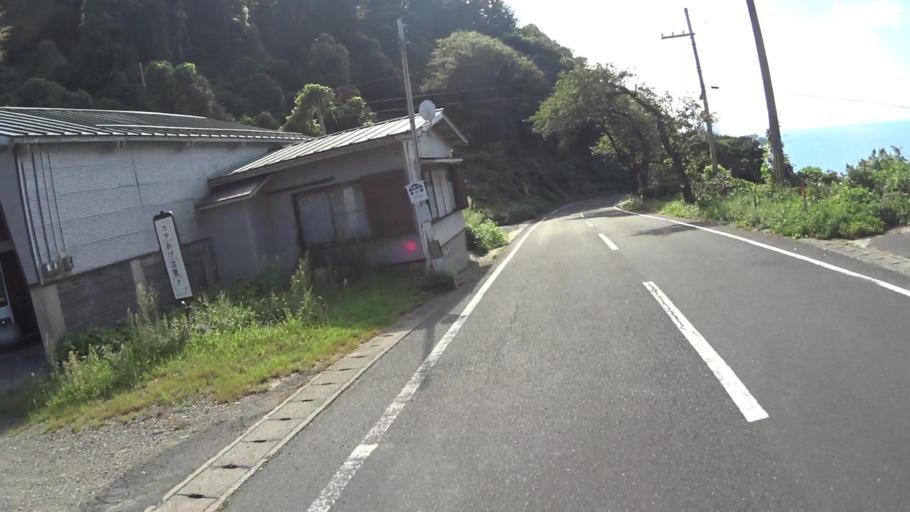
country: JP
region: Kyoto
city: Miyazu
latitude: 35.7692
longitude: 135.2203
